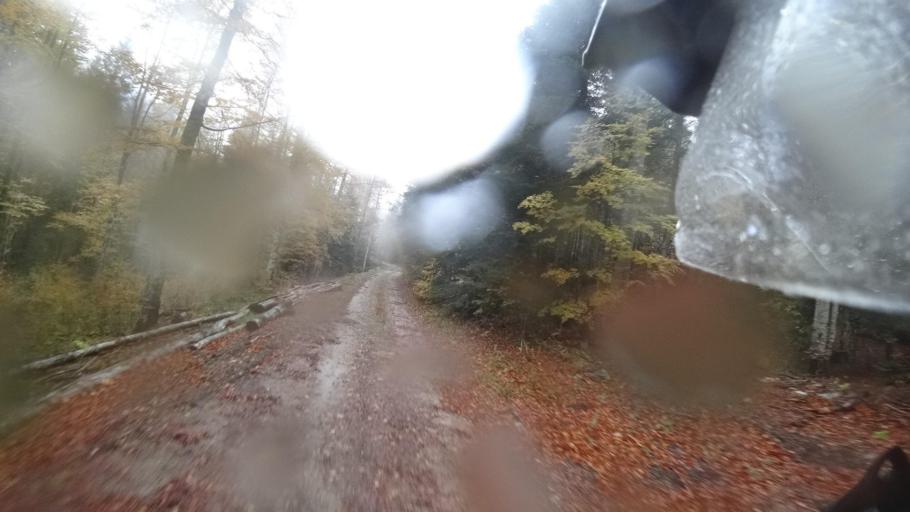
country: HR
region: Primorsko-Goranska
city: Vrbovsko
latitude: 45.2915
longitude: 14.9431
